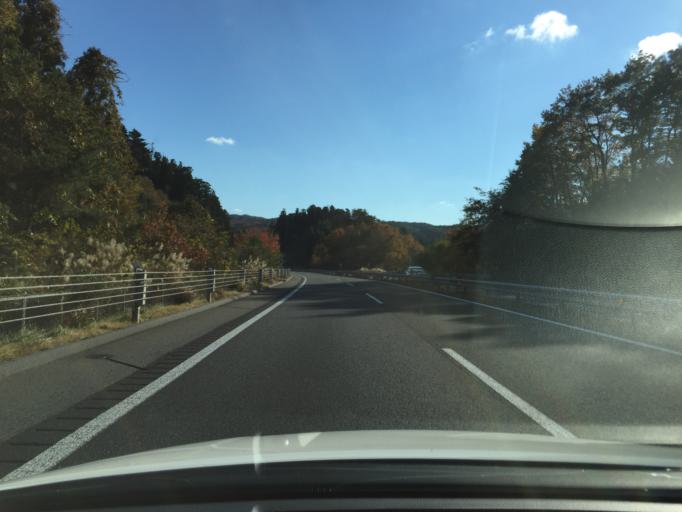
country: JP
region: Fukushima
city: Ishikawa
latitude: 37.2141
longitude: 140.6914
